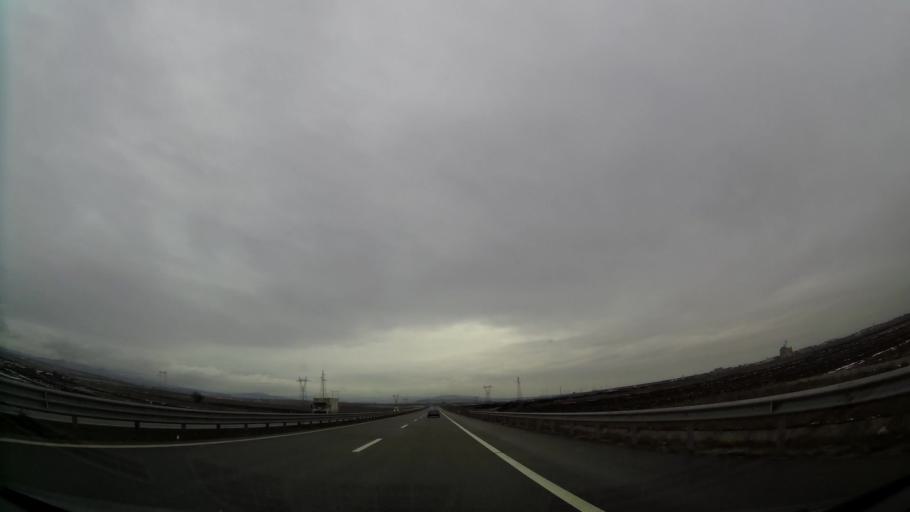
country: XK
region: Pristina
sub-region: Lipjan
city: Lipljan
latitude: 42.5184
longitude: 21.1712
